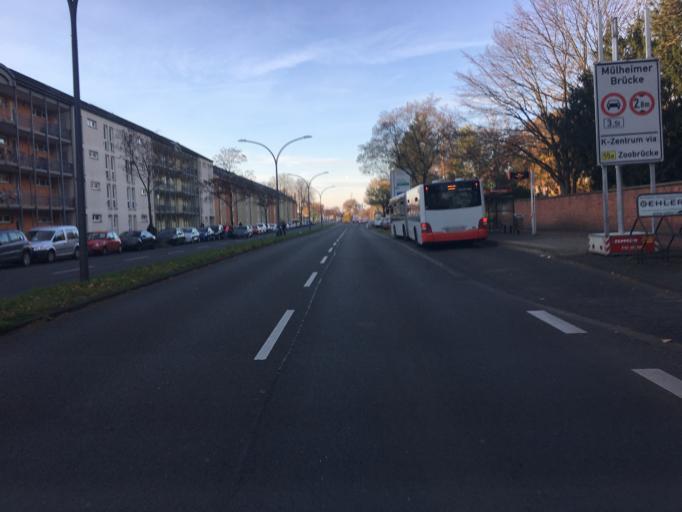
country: DE
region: North Rhine-Westphalia
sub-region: Regierungsbezirk Koln
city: Buchheim
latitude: 50.9466
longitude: 7.0225
